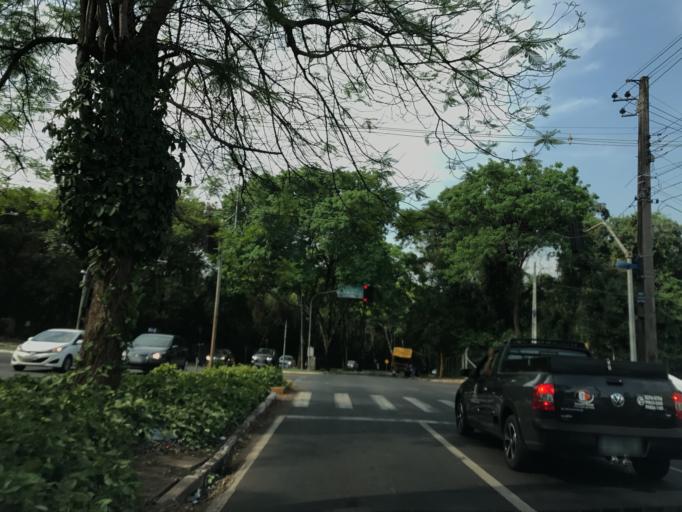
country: BR
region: Parana
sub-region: Maringa
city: Maringa
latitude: -23.4350
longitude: -51.9448
